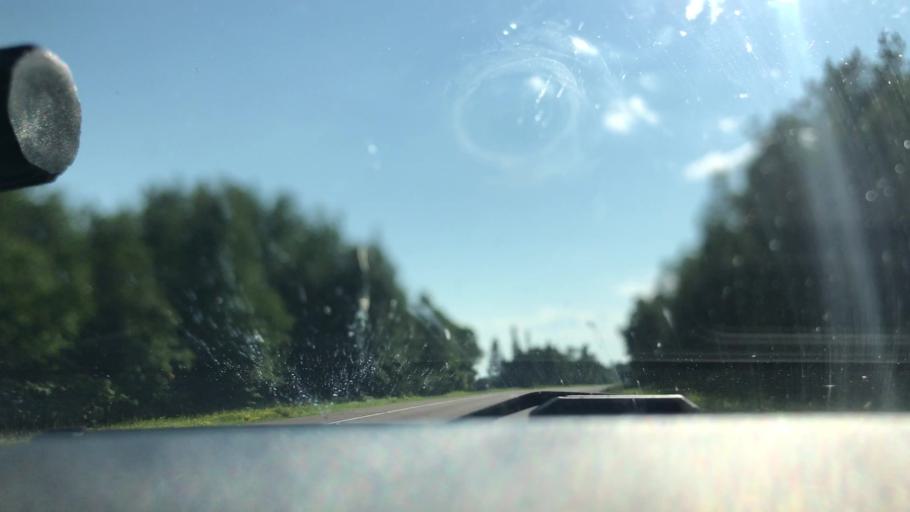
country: US
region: Minnesota
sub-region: Cook County
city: Grand Marais
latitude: 47.7982
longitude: -90.1079
